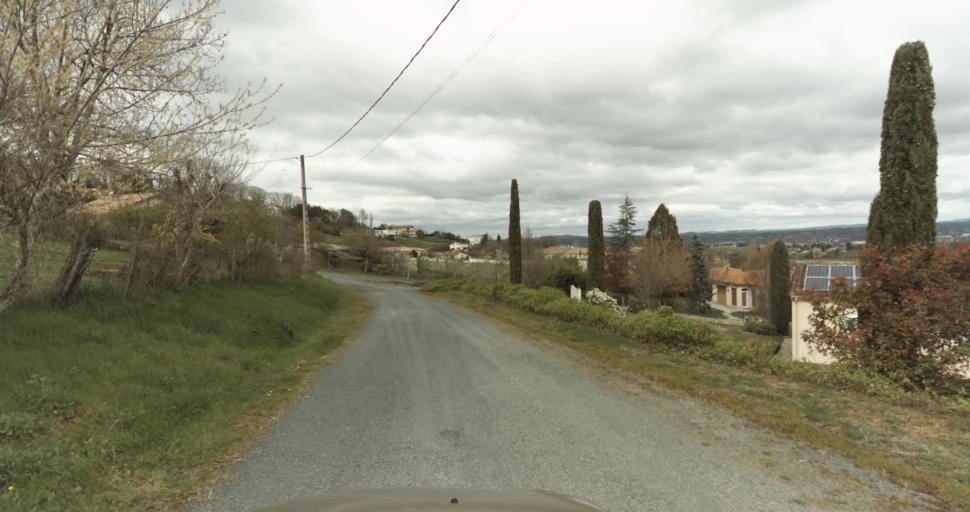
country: FR
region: Midi-Pyrenees
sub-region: Departement du Tarn
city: Puygouzon
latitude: 43.9030
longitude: 2.1680
